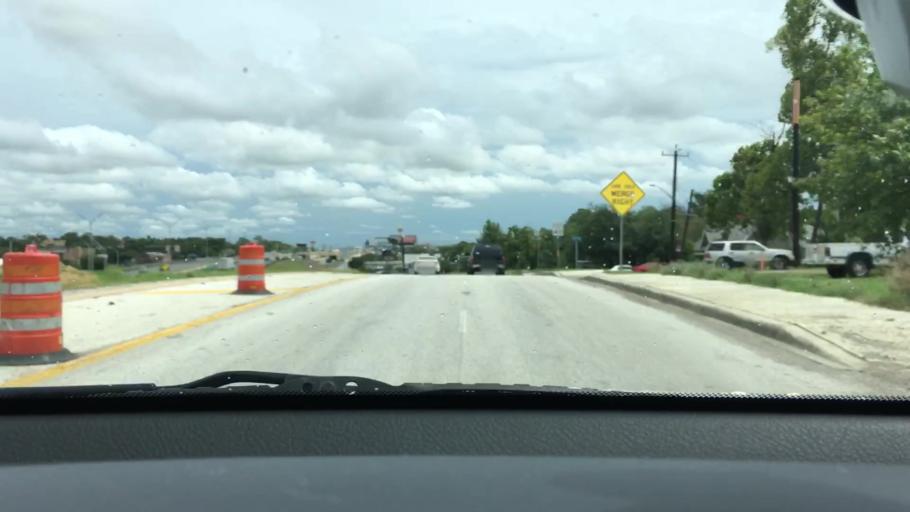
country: US
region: Texas
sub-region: Bexar County
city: San Antonio
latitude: 29.4379
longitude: -98.4602
